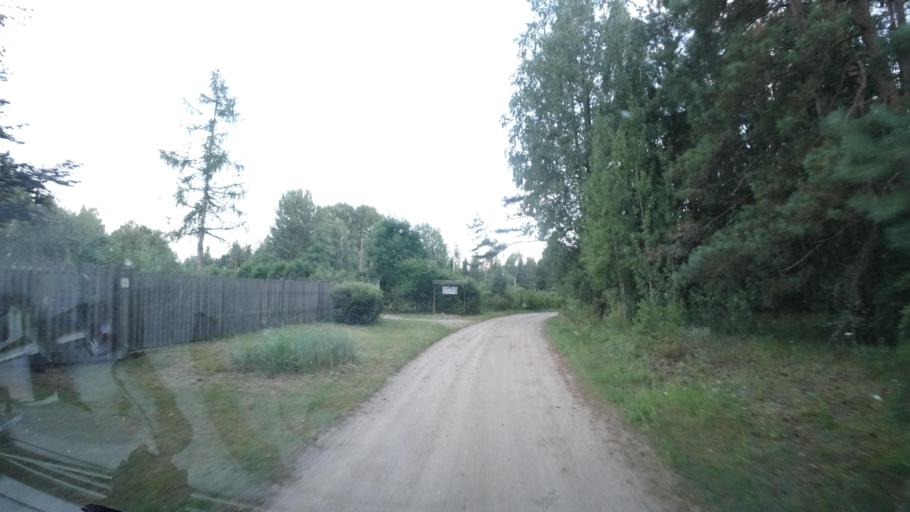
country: LT
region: Vilnius County
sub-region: Trakai
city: Rudiskes
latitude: 54.5079
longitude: 24.8895
